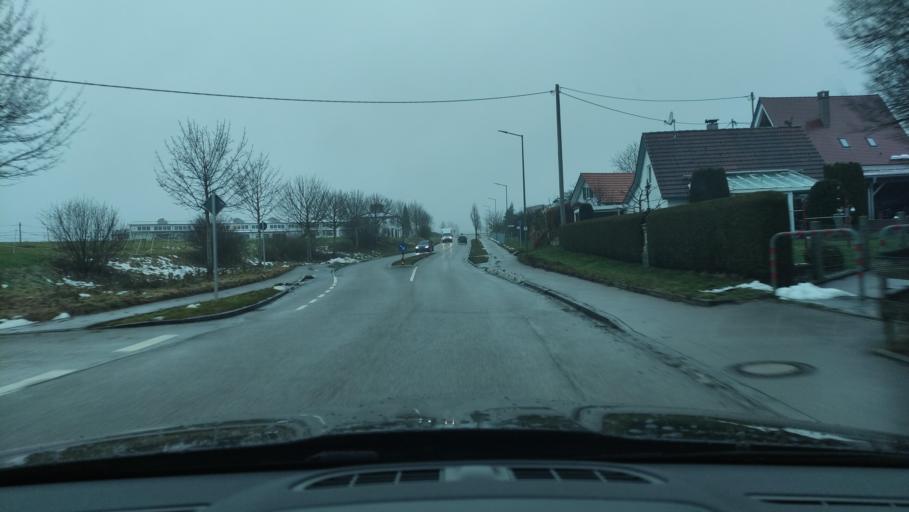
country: DE
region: Bavaria
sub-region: Swabia
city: Roggenburg
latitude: 48.2878
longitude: 10.2117
